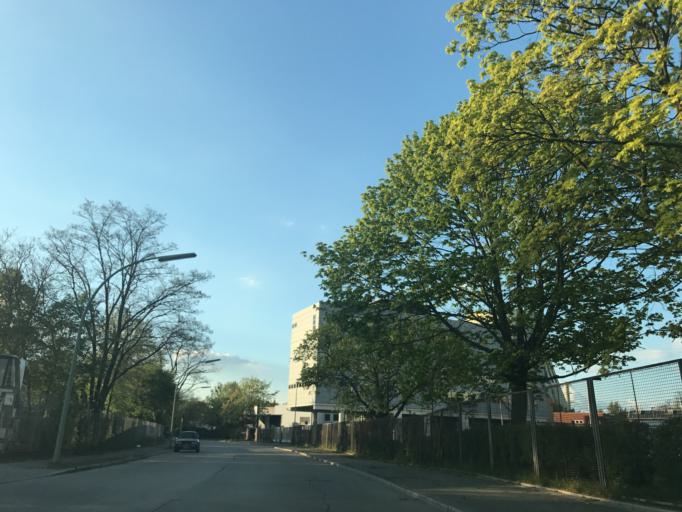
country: DE
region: Berlin
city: Haselhorst
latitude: 52.5304
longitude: 13.2372
